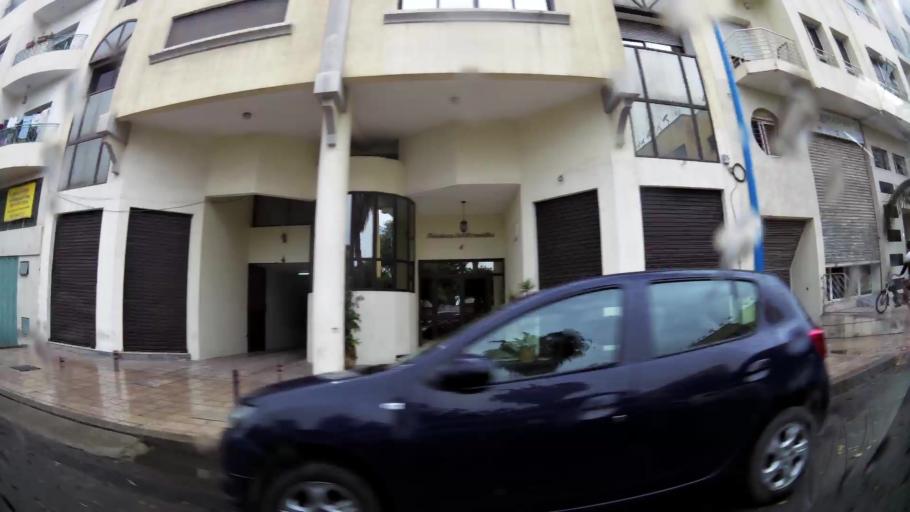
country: MA
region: Grand Casablanca
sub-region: Casablanca
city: Casablanca
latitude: 33.5766
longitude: -7.6137
